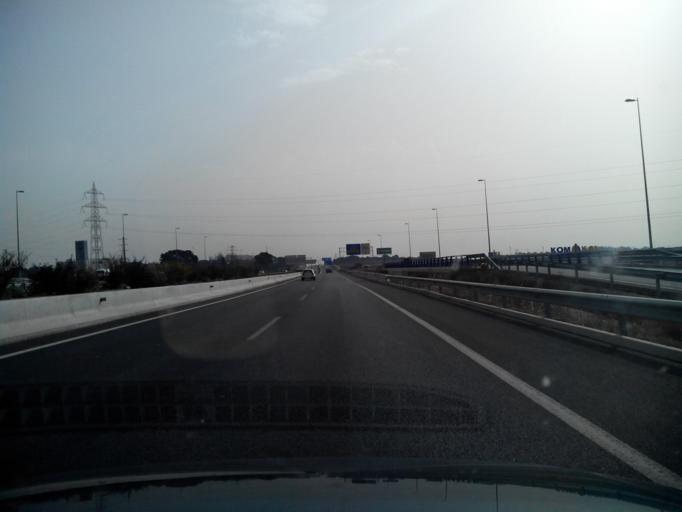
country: ES
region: Catalonia
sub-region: Provincia de Tarragona
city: Vila-seca
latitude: 41.1352
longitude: 1.1761
